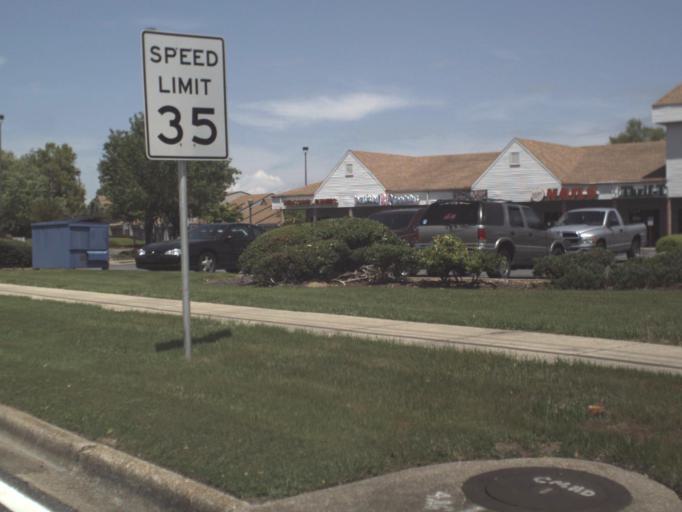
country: US
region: Florida
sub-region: Escambia County
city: Goulding
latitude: 30.4665
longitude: -87.2046
